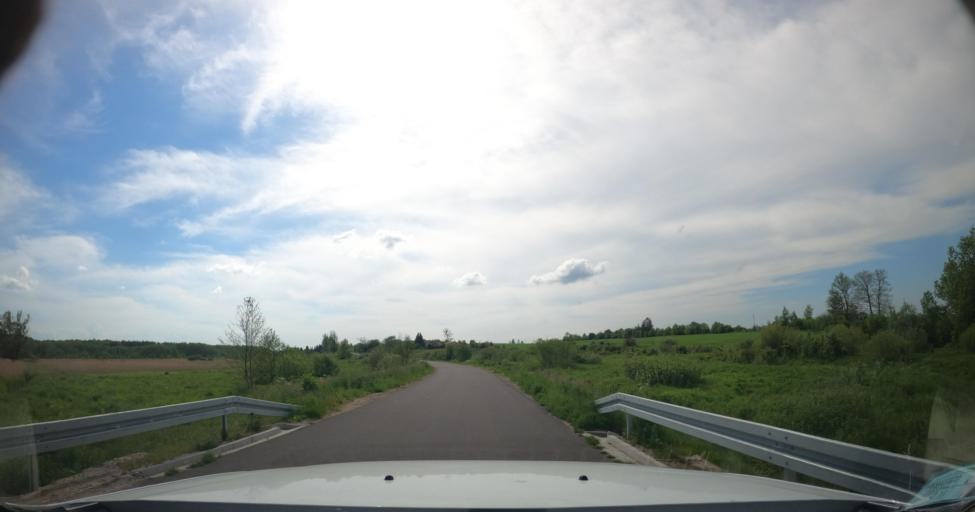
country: PL
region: Warmian-Masurian Voivodeship
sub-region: Powiat lidzbarski
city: Lidzbark Warminski
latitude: 54.1234
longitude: 20.5273
